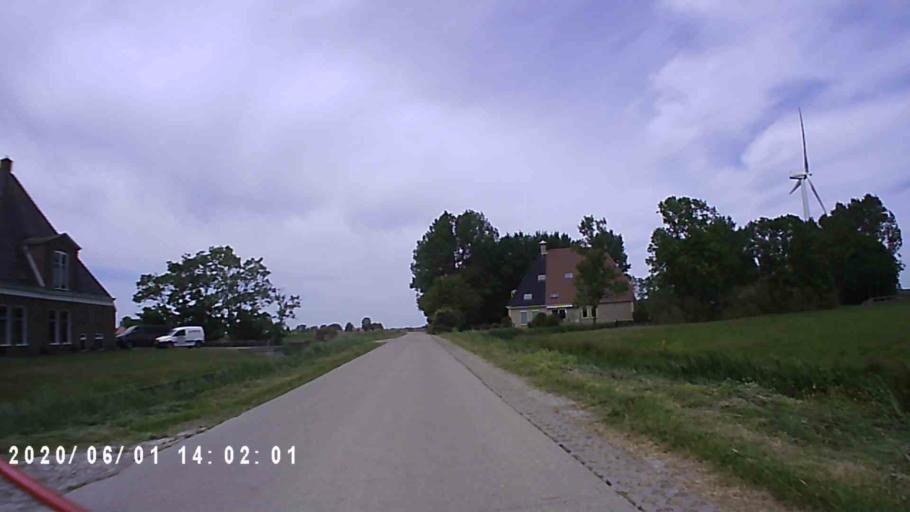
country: NL
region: Friesland
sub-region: Gemeente Littenseradiel
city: Makkum
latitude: 53.1102
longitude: 5.6422
